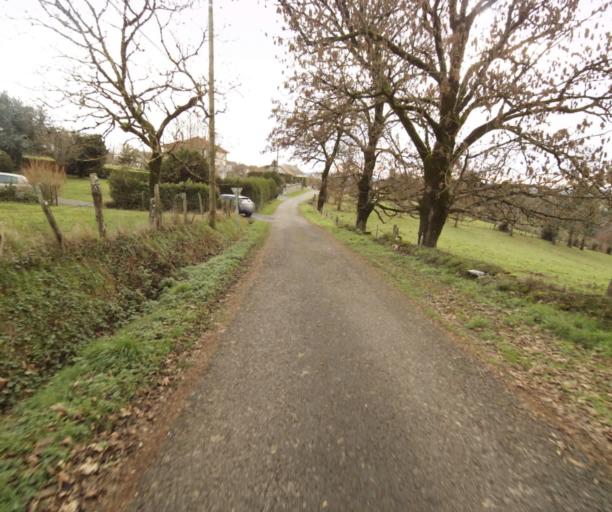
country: FR
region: Limousin
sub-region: Departement de la Correze
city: Chameyrat
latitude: 45.2642
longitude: 1.7223
